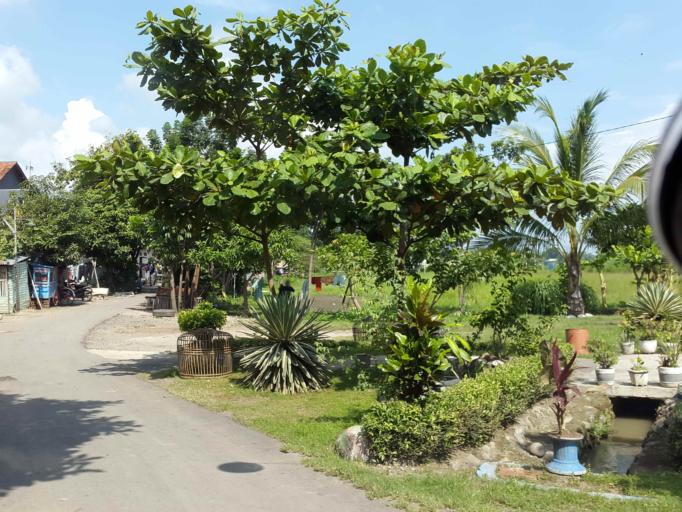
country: ID
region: Central Java
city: Pemalang
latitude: -6.8864
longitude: 109.3911
